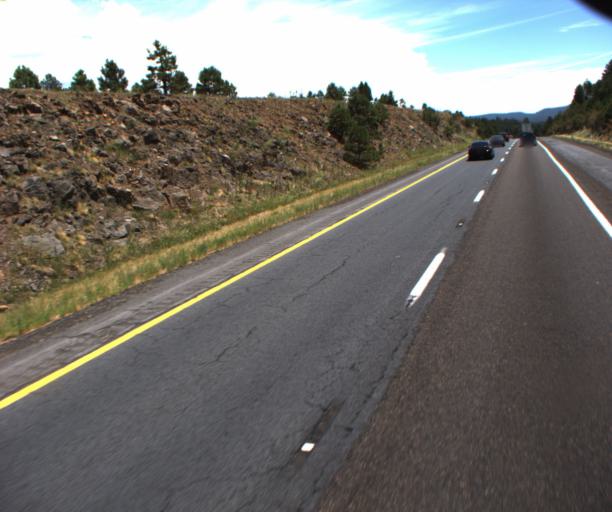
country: US
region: Arizona
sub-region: Coconino County
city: Parks
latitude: 35.2541
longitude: -112.0070
